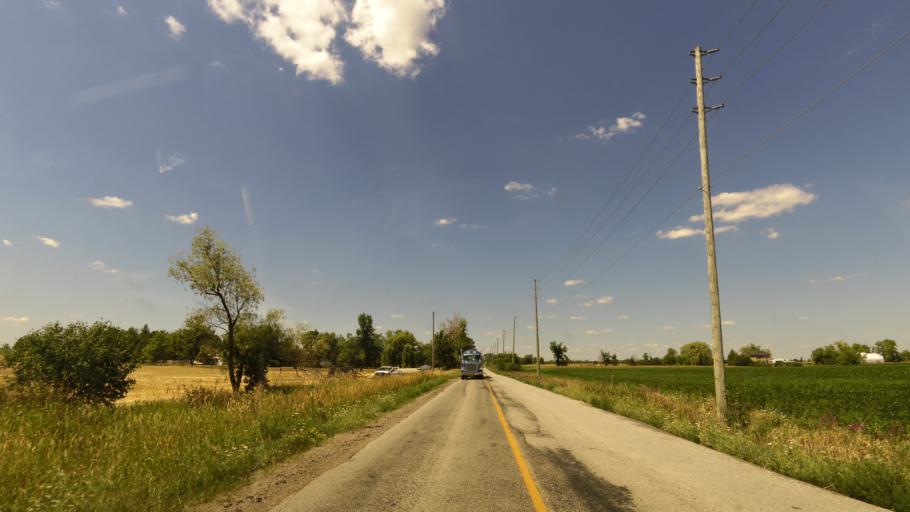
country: CA
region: Ontario
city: Brampton
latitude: 43.6063
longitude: -79.8200
